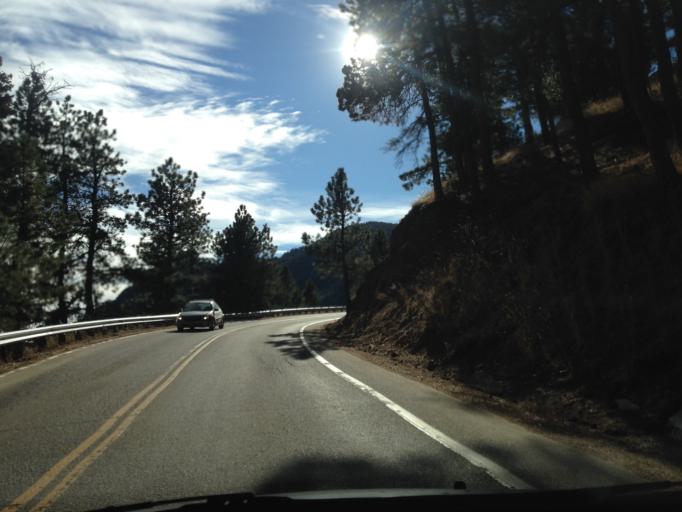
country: US
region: Colorado
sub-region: Boulder County
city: Boulder
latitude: 40.0022
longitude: -105.2999
